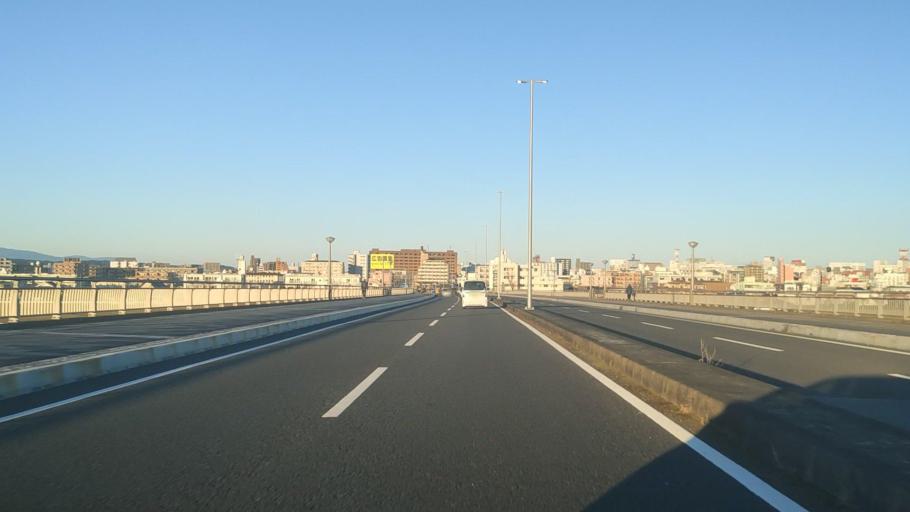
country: JP
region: Miyazaki
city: Miyazaki-shi
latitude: 31.9082
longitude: 131.4113
